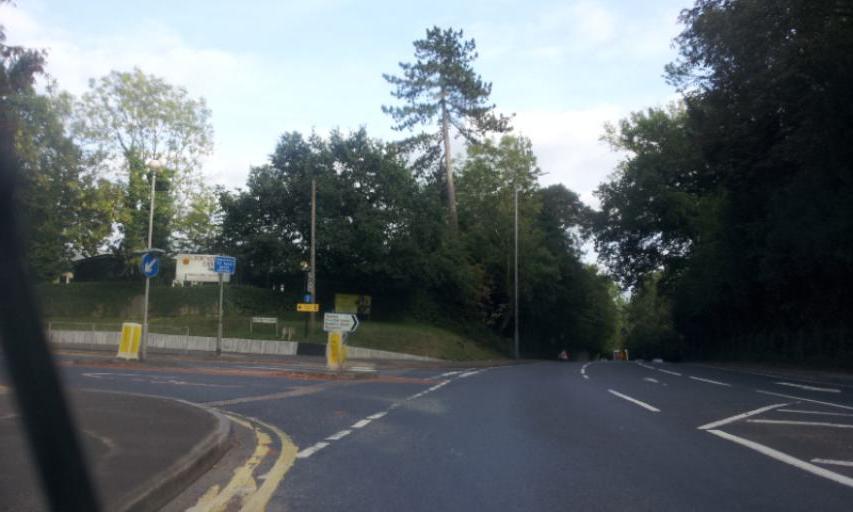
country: GB
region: England
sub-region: Kent
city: Tonbridge
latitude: 51.1848
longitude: 0.2788
